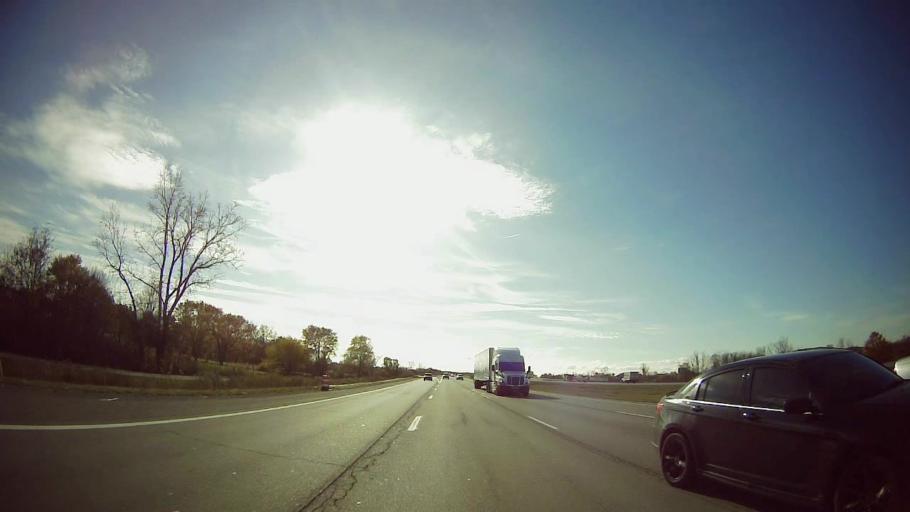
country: US
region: Michigan
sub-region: Wayne County
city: Canton
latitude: 42.2849
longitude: -83.4427
